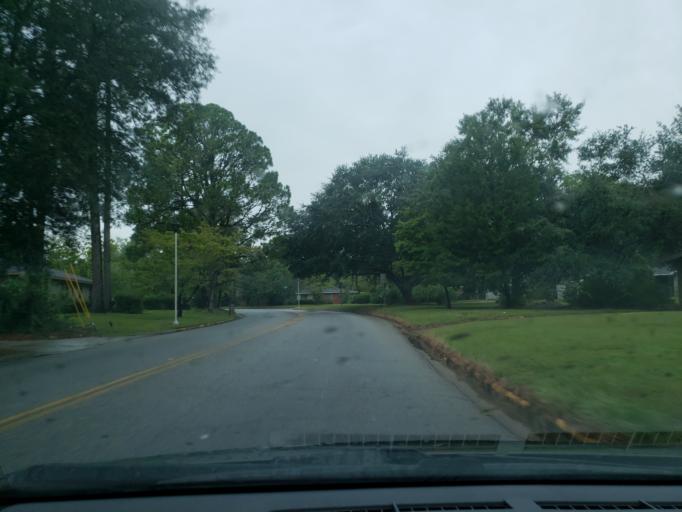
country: US
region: Georgia
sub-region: Dougherty County
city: Albany
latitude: 31.6053
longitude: -84.1943
